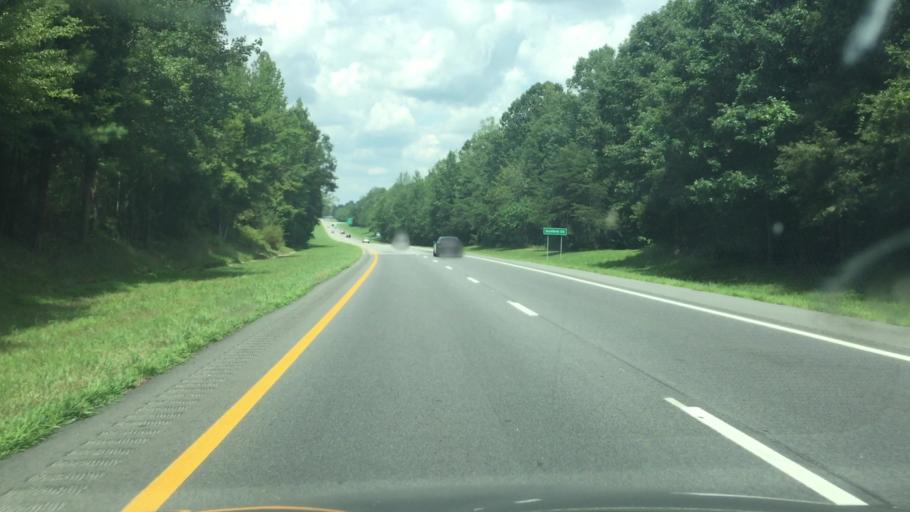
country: US
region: North Carolina
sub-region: Guilford County
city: Pleasant Garden
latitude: 35.9106
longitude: -79.8217
